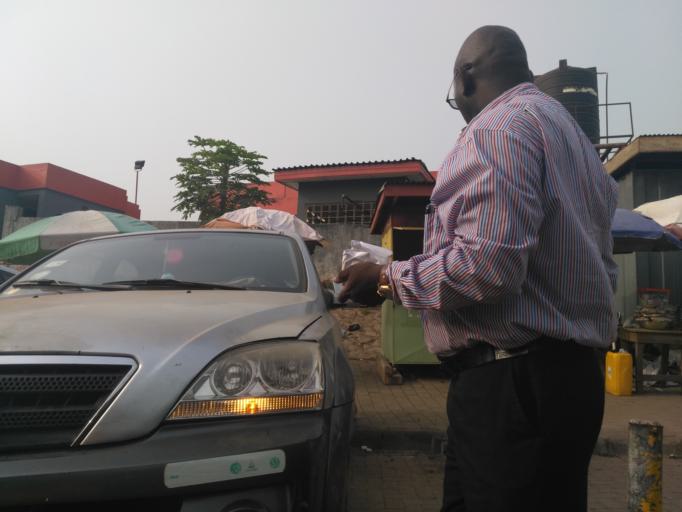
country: GH
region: Ashanti
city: Kumasi
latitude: 6.6886
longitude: -1.6148
